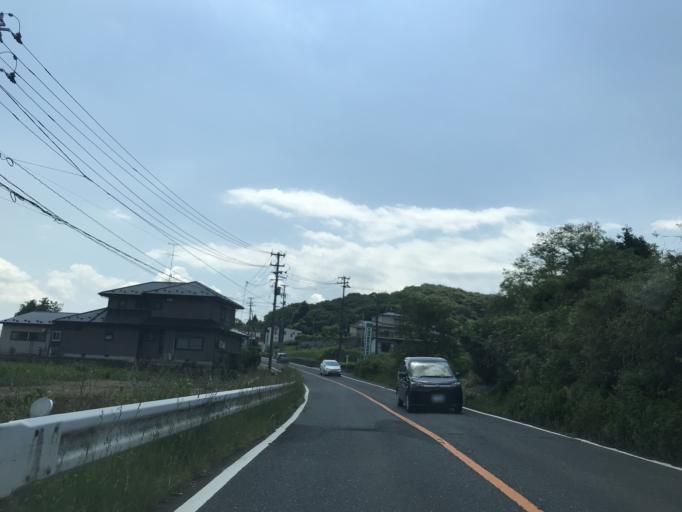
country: JP
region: Miyagi
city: Wakuya
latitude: 38.4895
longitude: 141.0887
